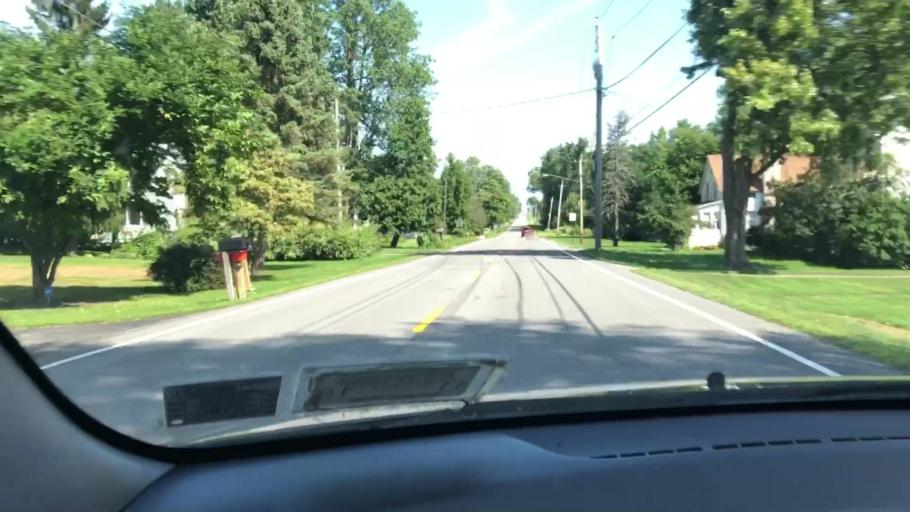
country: US
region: New York
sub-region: Wayne County
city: Macedon
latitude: 43.0964
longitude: -77.3206
